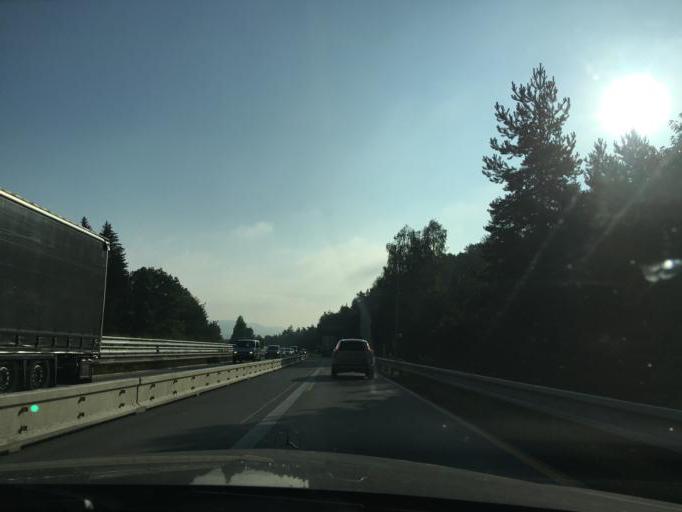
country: CZ
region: Central Bohemia
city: Trhovy Stepanov
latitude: 49.7493
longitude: 14.9926
